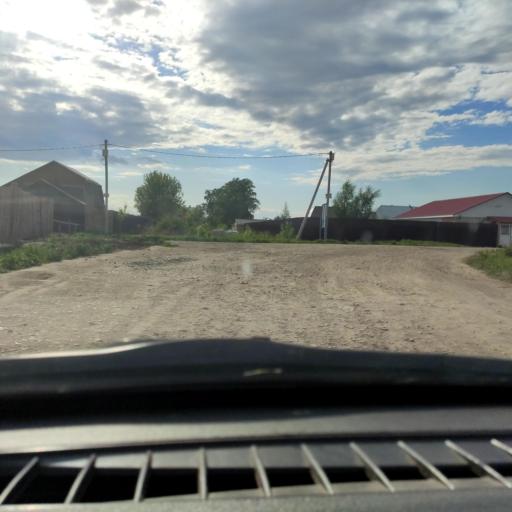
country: RU
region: Samara
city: Tol'yatti
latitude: 53.5688
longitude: 49.4091
